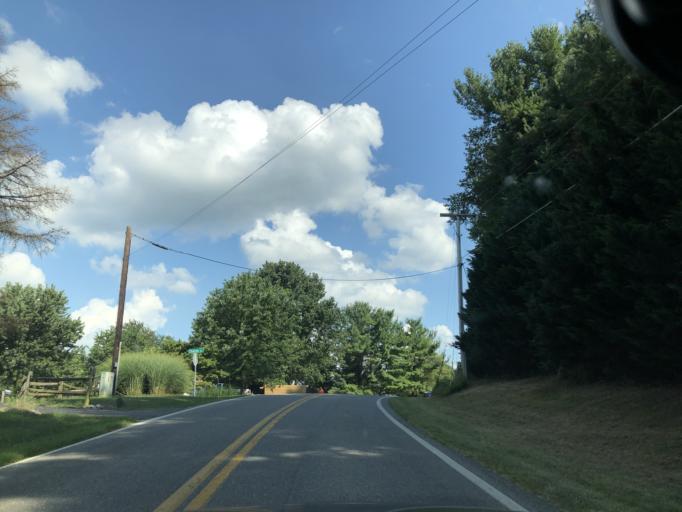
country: US
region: Maryland
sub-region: Frederick County
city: Linganore
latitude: 39.4146
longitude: -77.2074
